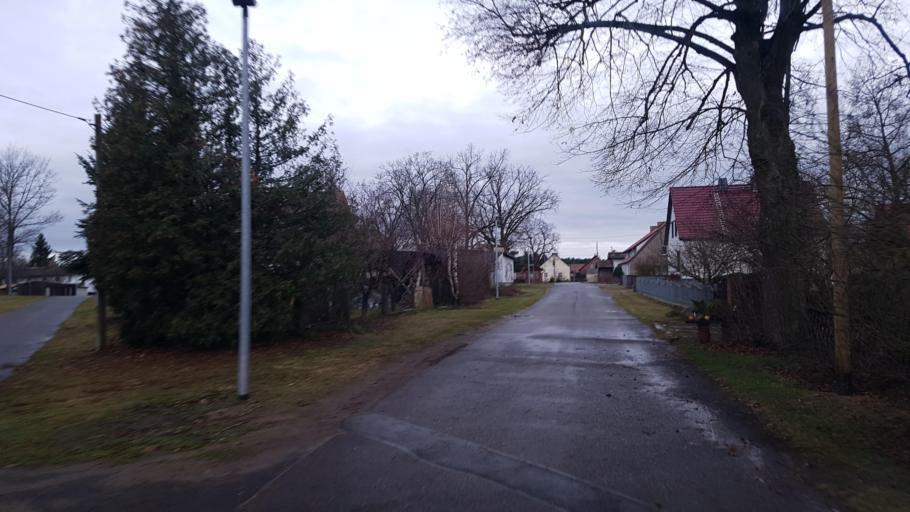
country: DE
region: Brandenburg
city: Tauche
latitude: 52.0682
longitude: 14.0979
